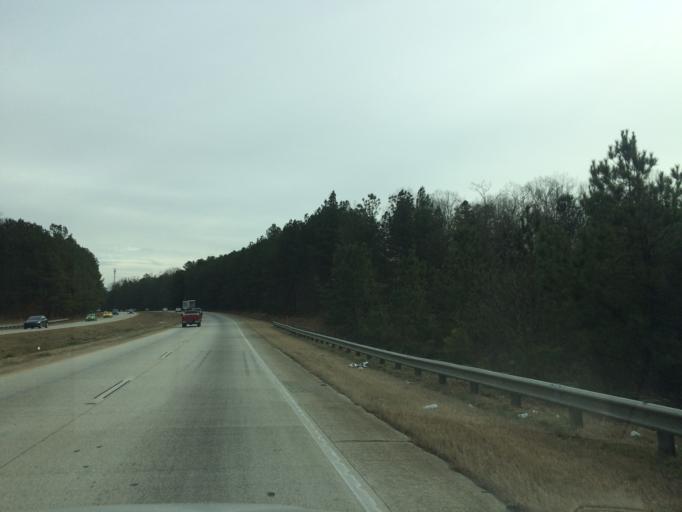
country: US
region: Georgia
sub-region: Gwinnett County
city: Dacula
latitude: 33.9776
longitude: -83.9210
